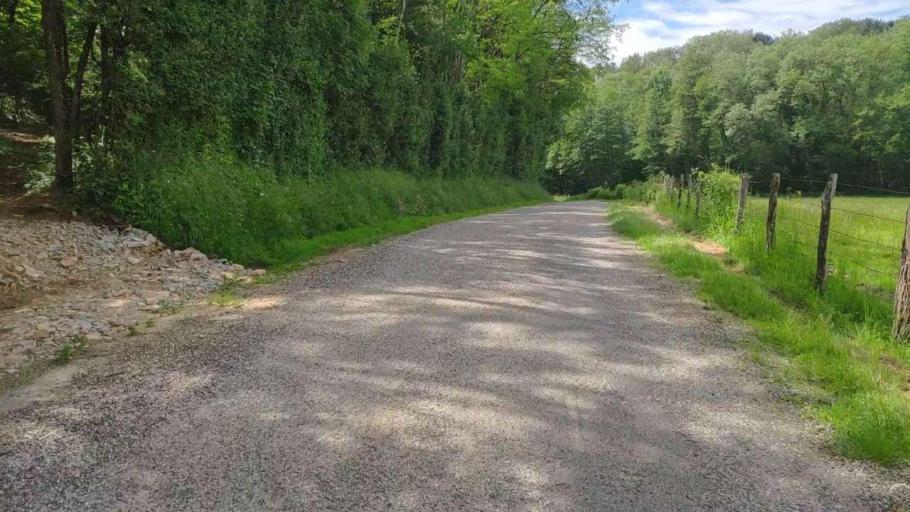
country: FR
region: Franche-Comte
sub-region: Departement du Jura
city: Montmorot
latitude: 46.7434
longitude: 5.5384
